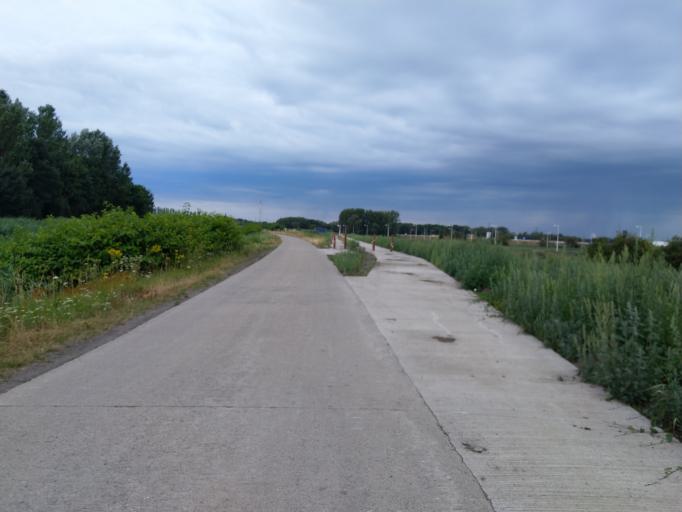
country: BE
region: Wallonia
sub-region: Province du Hainaut
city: Mons
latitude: 50.4538
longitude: 3.9208
